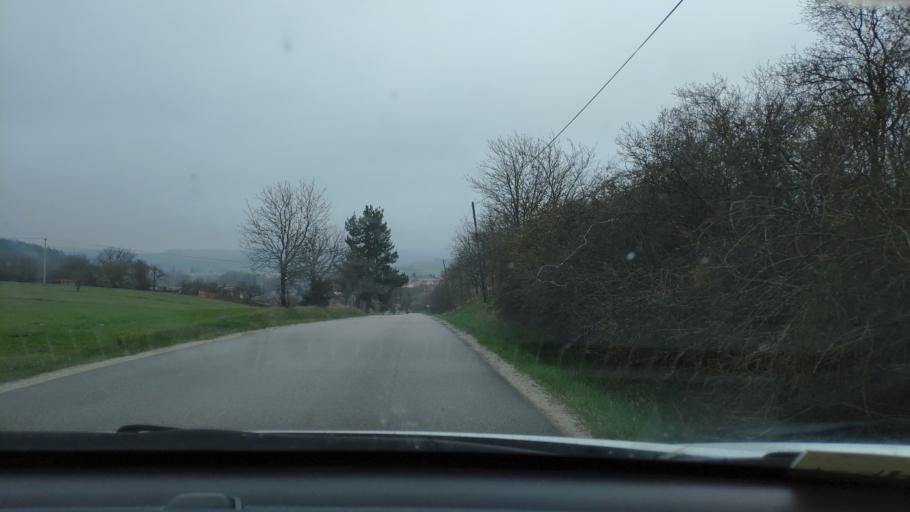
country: CZ
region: Vysocina
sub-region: Okres Jihlava
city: Telc
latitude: 49.1943
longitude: 15.3819
